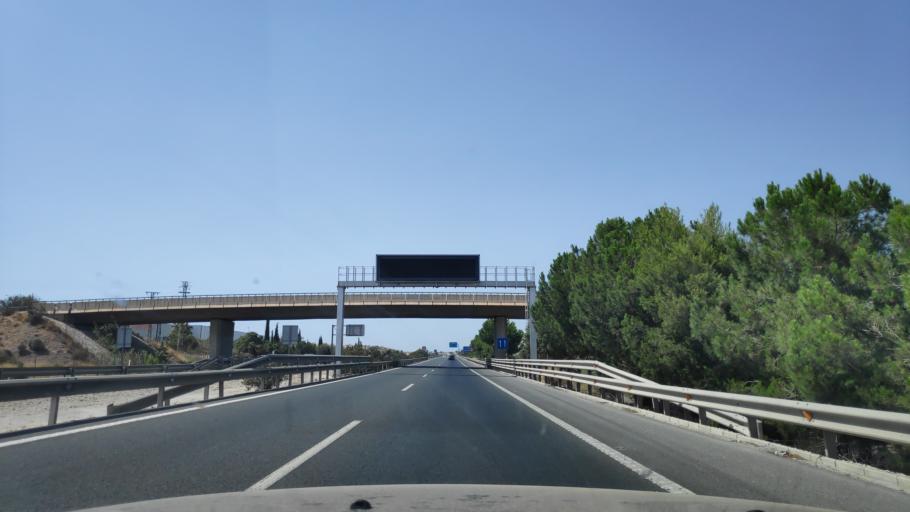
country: ES
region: Murcia
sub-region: Murcia
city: Lorqui
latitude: 38.0889
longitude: -1.2241
